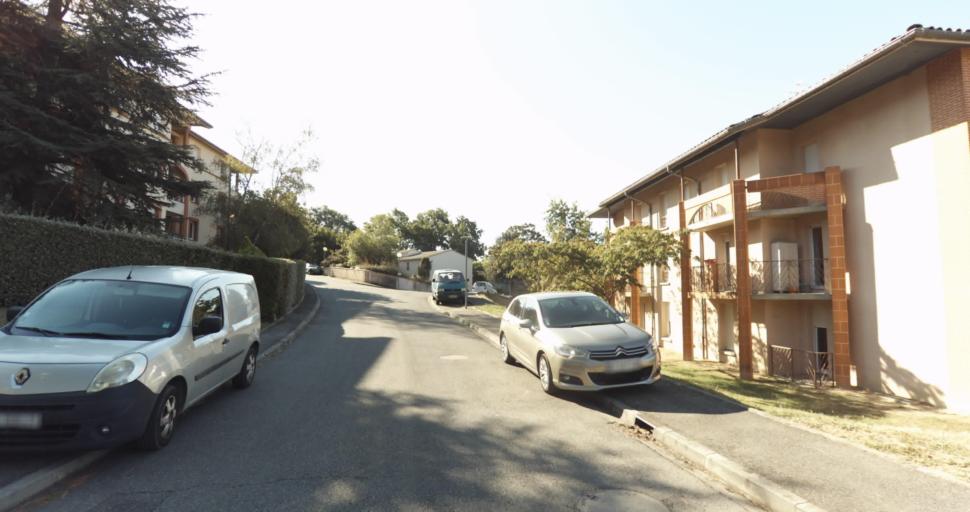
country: FR
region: Midi-Pyrenees
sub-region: Departement de la Haute-Garonne
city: L'Union
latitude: 43.6642
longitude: 1.4809
